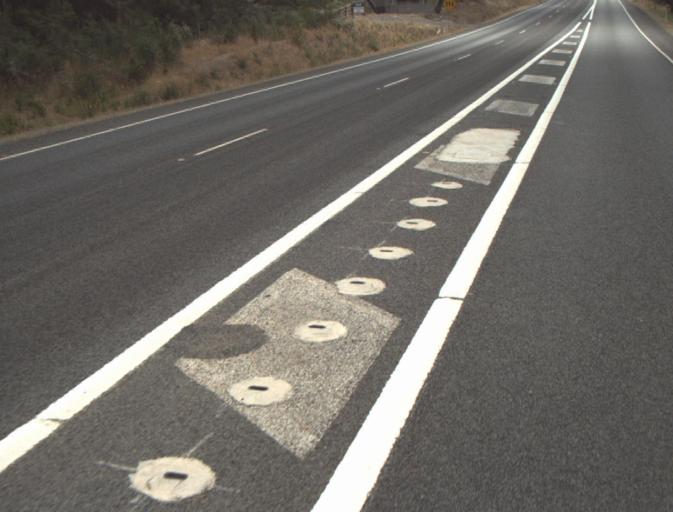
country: AU
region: Tasmania
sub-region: Launceston
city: Mayfield
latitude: -41.2891
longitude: 147.0428
